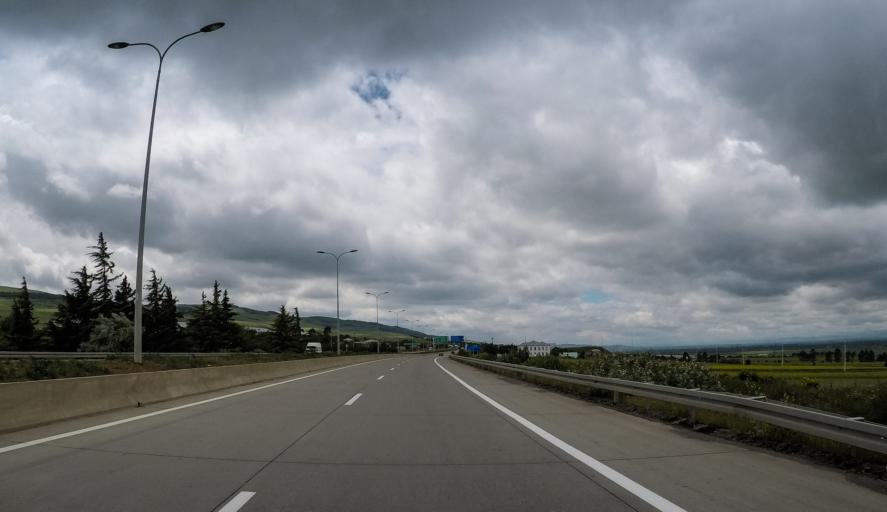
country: GE
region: Shida Kartli
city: Gori
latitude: 42.0240
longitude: 44.2534
